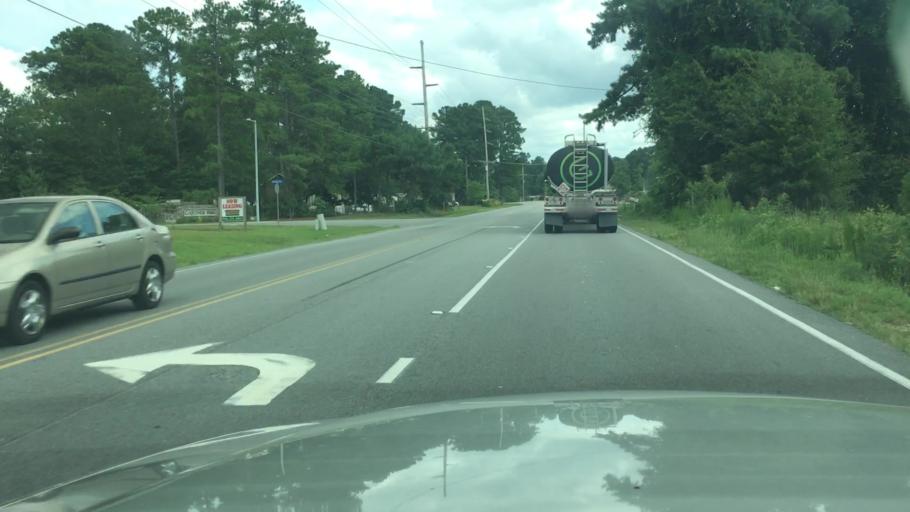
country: US
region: North Carolina
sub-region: Hoke County
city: Rockfish
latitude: 35.0107
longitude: -79.0034
